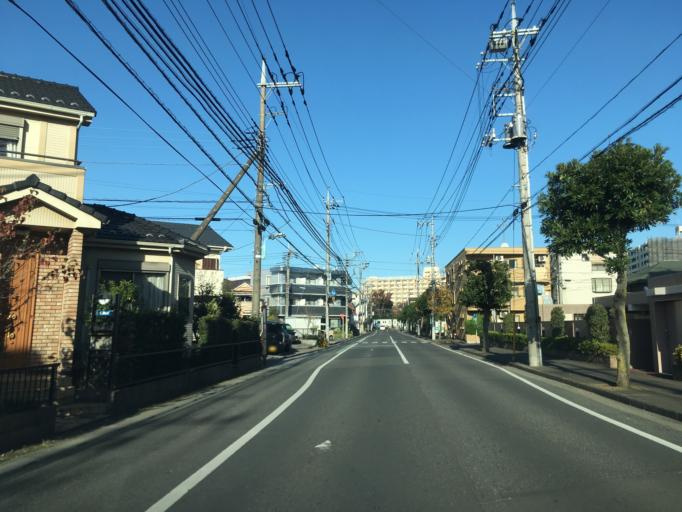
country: JP
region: Saitama
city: Tokorozawa
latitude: 35.7993
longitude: 139.4613
